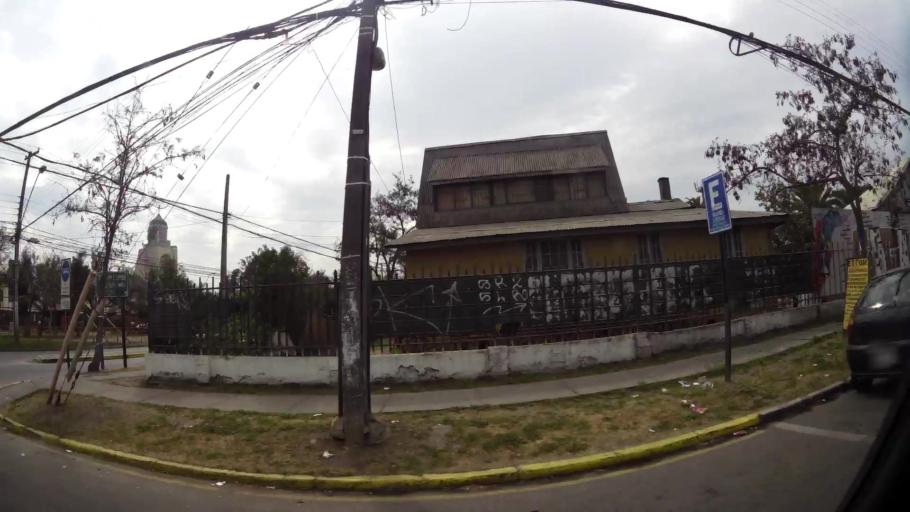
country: CL
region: Santiago Metropolitan
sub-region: Provincia de Santiago
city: Lo Prado
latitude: -33.5132
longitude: -70.7631
